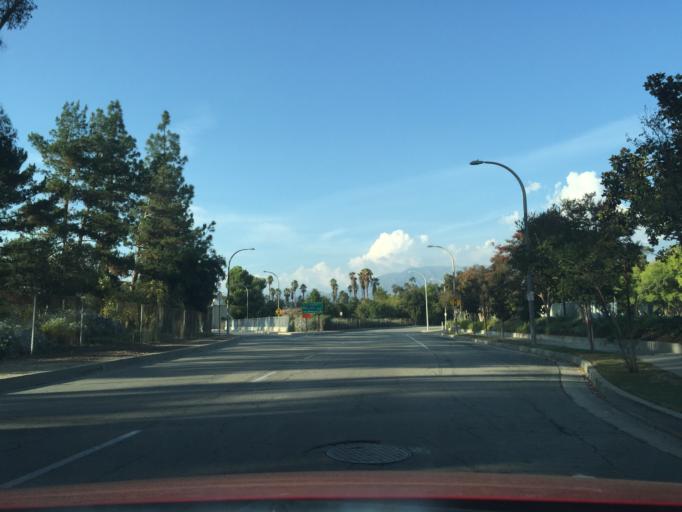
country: US
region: California
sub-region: Los Angeles County
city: Pasadena
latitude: 34.1479
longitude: -118.1542
